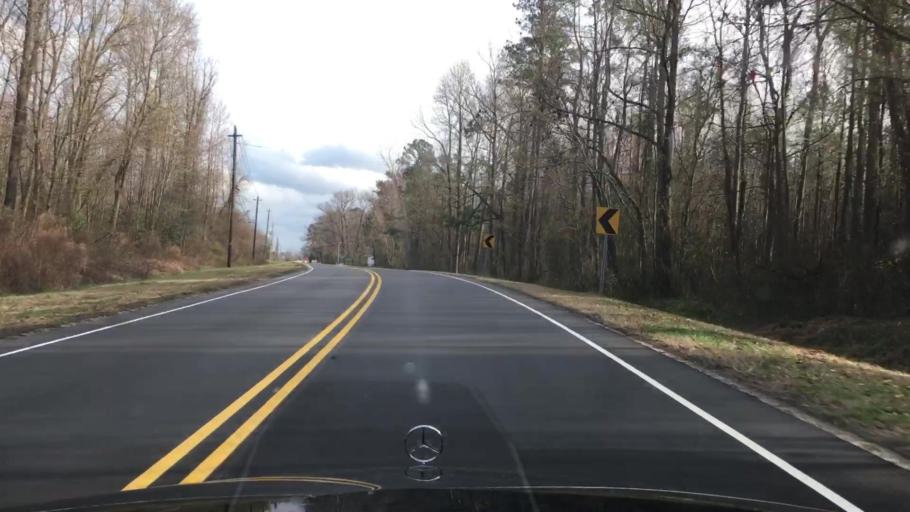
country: US
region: North Carolina
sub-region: Duplin County
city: Kenansville
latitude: 34.9613
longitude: -77.9925
